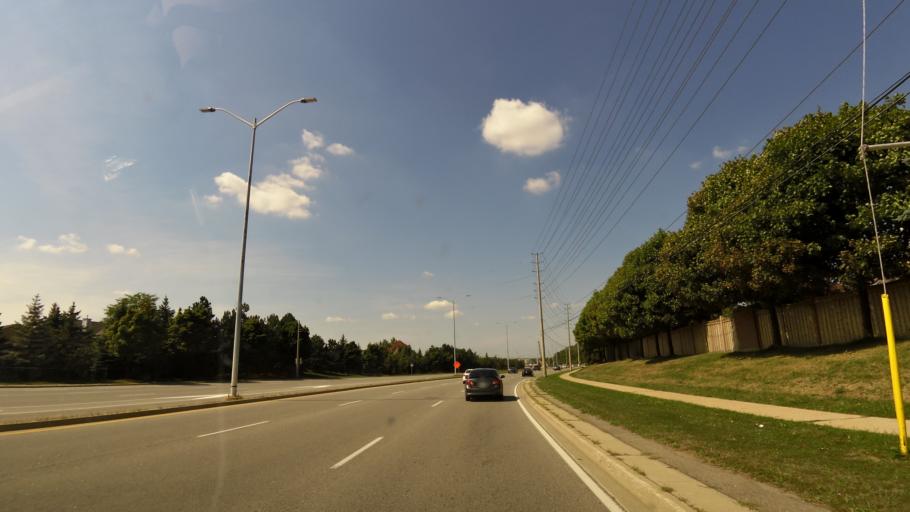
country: CA
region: Ontario
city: Mississauga
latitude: 43.5737
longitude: -79.7279
